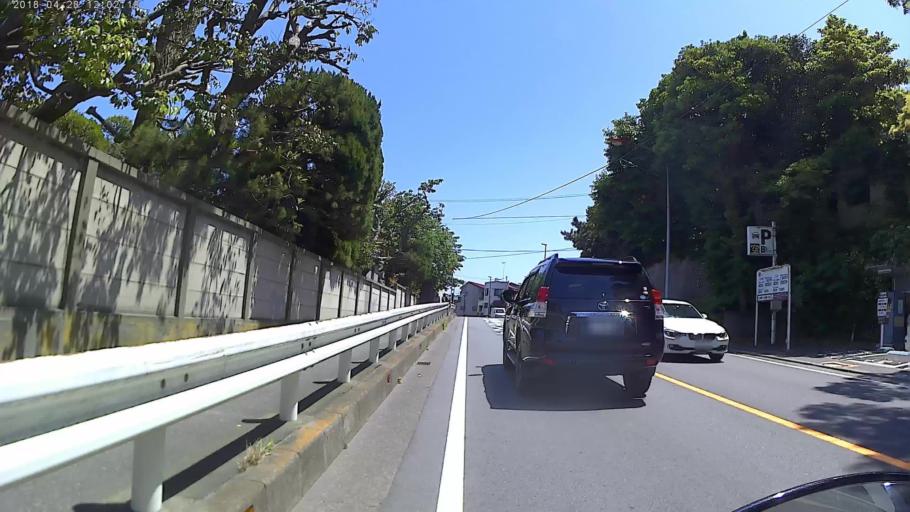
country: JP
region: Kanagawa
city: Fujisawa
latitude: 35.3072
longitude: 139.4934
